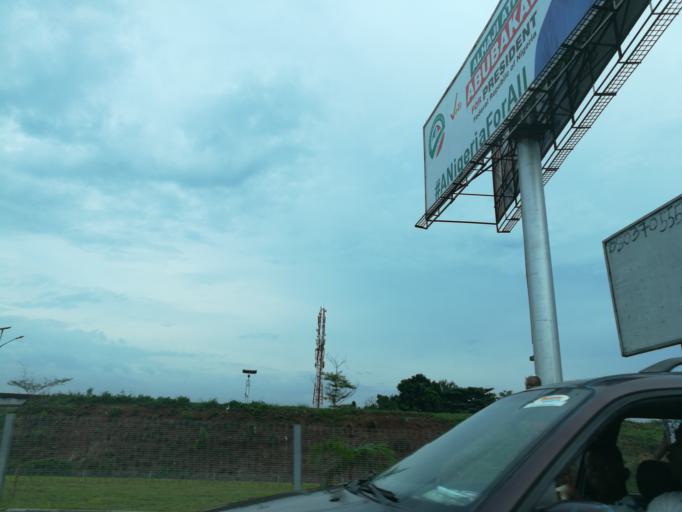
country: NG
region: Rivers
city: Port Harcourt
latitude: 4.8096
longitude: 7.0161
